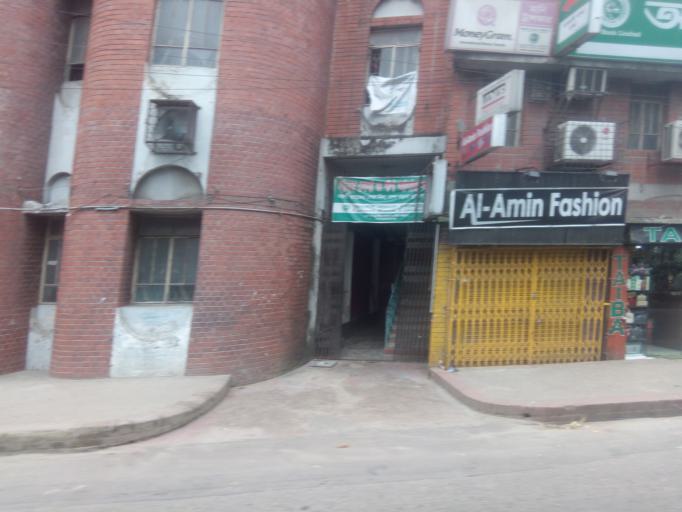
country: BD
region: Dhaka
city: Azimpur
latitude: 23.7545
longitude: 90.3765
